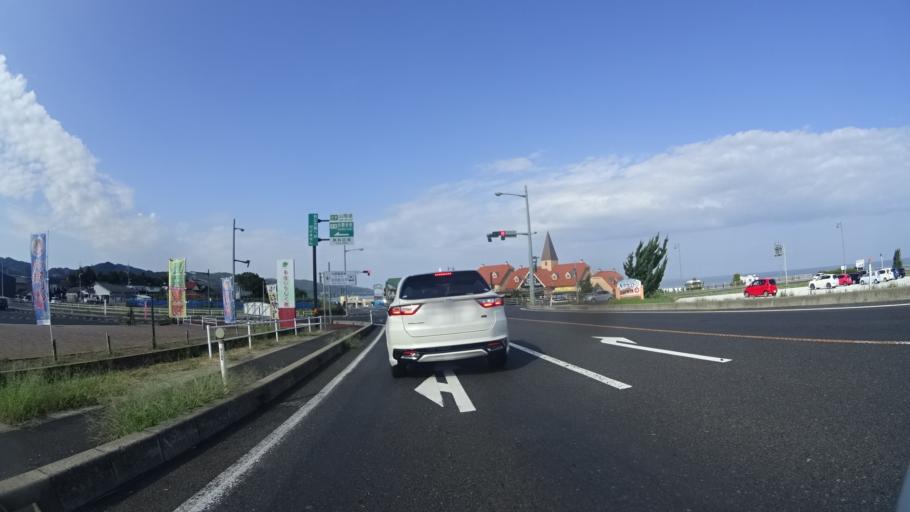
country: JP
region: Shimane
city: Izumo
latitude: 35.2907
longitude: 132.6341
